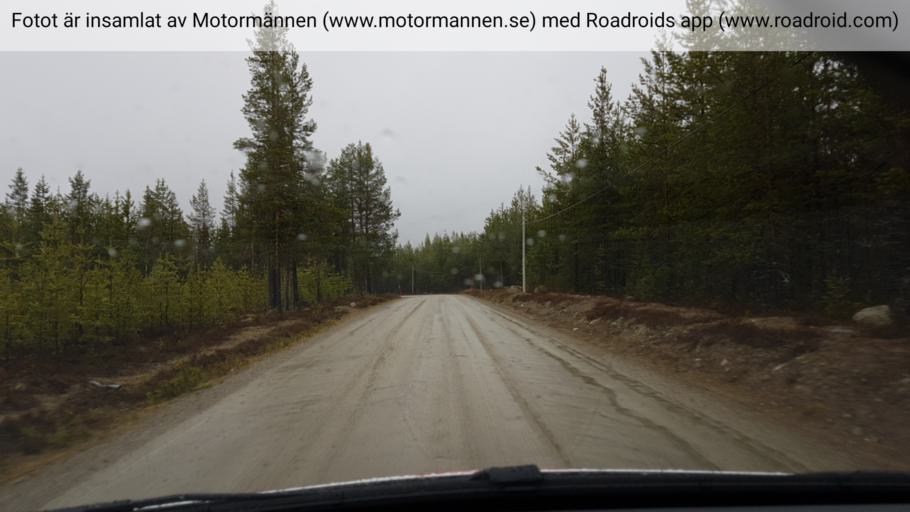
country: SE
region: Jaemtland
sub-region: Are Kommun
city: Jarpen
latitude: 62.4903
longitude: 13.5096
